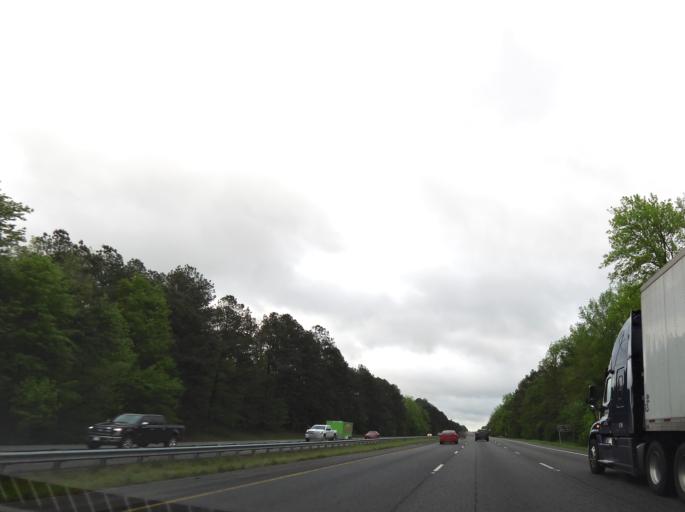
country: US
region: Georgia
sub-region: Monroe County
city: Forsyth
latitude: 33.0787
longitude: -83.9863
